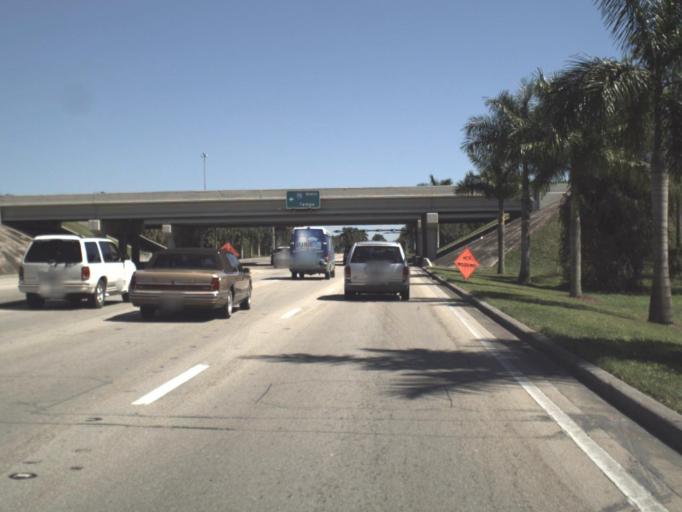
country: US
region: Florida
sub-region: Collier County
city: Vineyards
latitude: 26.2115
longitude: -81.7373
